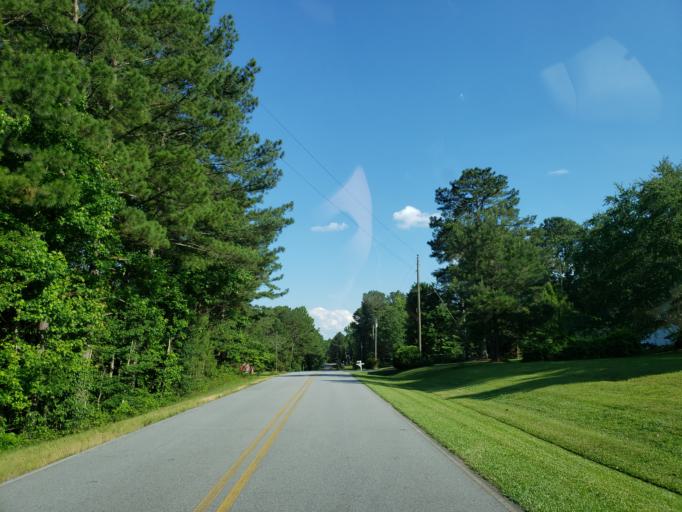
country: US
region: Georgia
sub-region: Haralson County
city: Bremen
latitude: 33.6786
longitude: -85.0862
